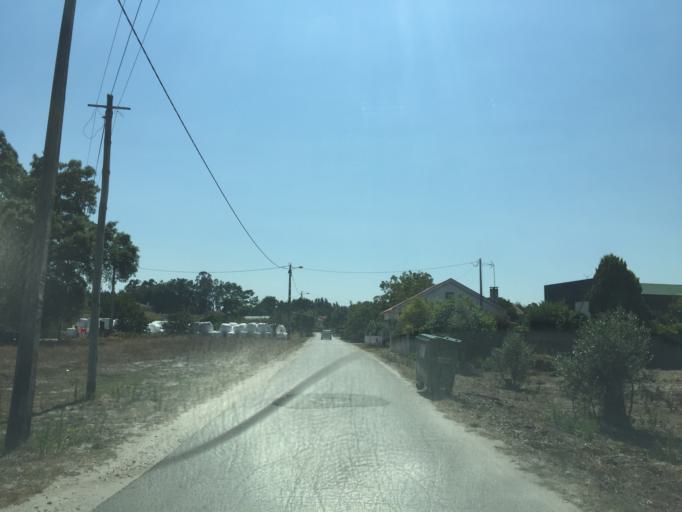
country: PT
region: Coimbra
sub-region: Mira
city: Mira
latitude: 40.3405
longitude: -8.7278
